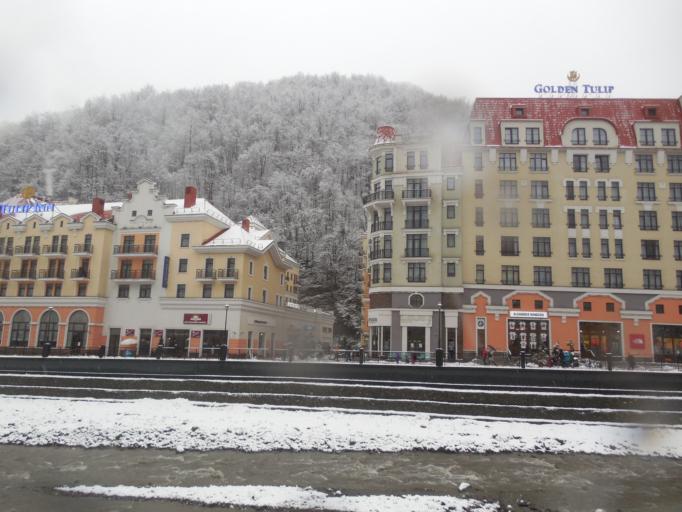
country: RU
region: Krasnodarskiy
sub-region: Sochi City
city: Krasnaya Polyana
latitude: 43.6718
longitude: 40.2943
